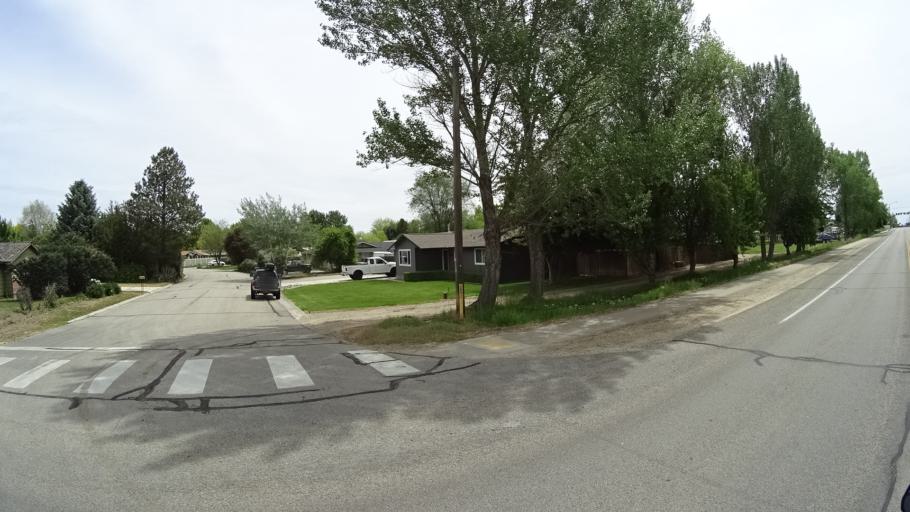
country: US
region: Idaho
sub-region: Ada County
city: Meridian
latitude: 43.5559
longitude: -116.3343
